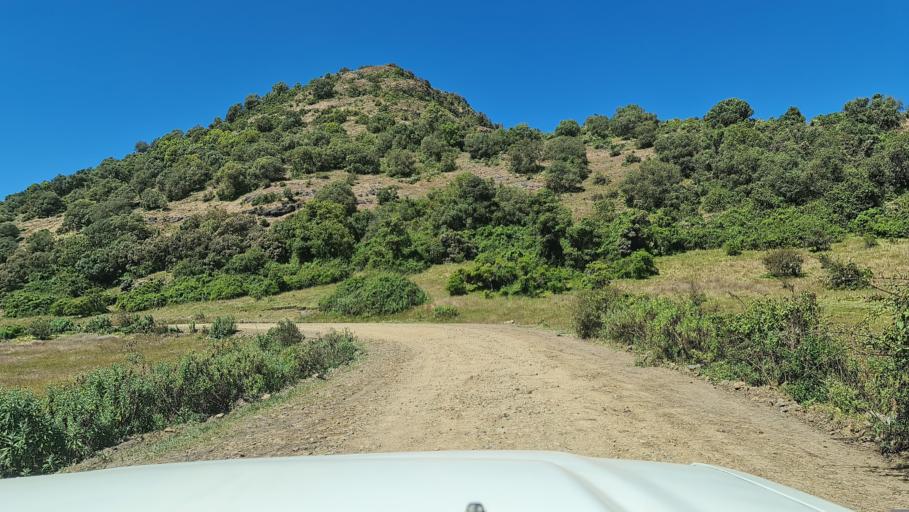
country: ET
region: Amhara
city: Debark'
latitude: 13.2355
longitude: 38.0661
